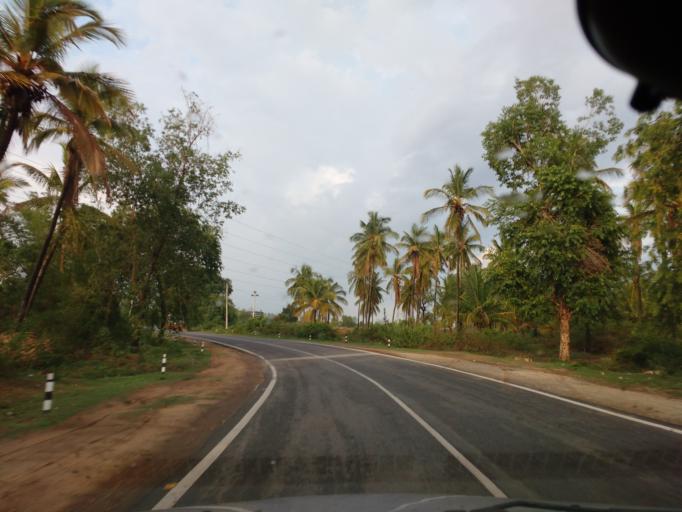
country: IN
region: Karnataka
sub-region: Tumkur
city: Tiptur
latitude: 13.2666
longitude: 76.4010
